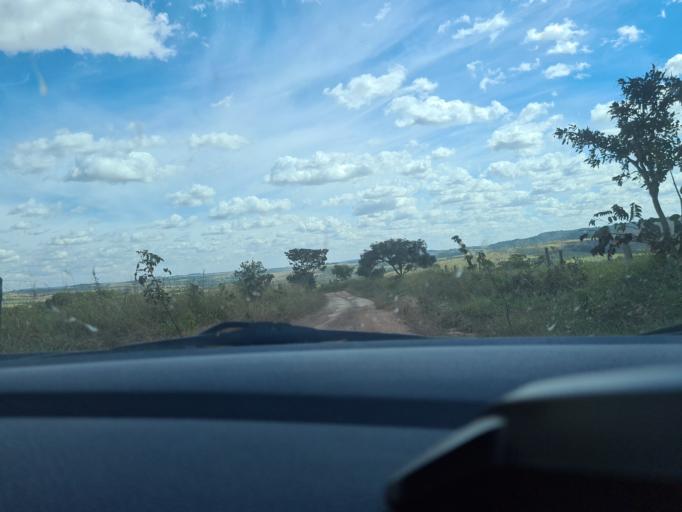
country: BR
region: Goias
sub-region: Silvania
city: Silvania
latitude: -16.5421
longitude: -48.5705
